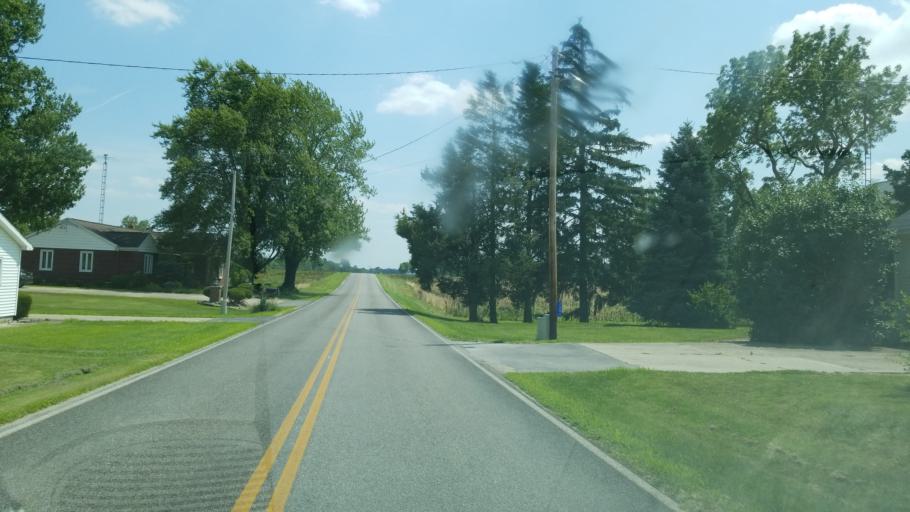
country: US
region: Ohio
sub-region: Seneca County
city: Tiffin
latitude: 41.1570
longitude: -83.2040
